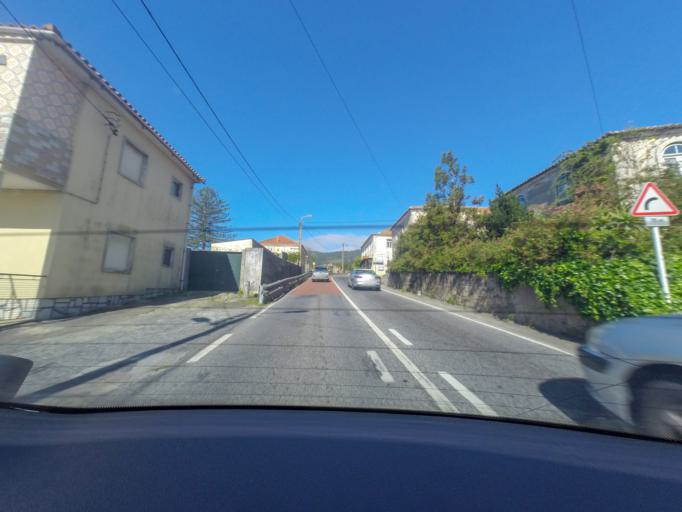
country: PT
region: Lisbon
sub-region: Sintra
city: Sintra
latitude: 38.7837
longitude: -9.3695
